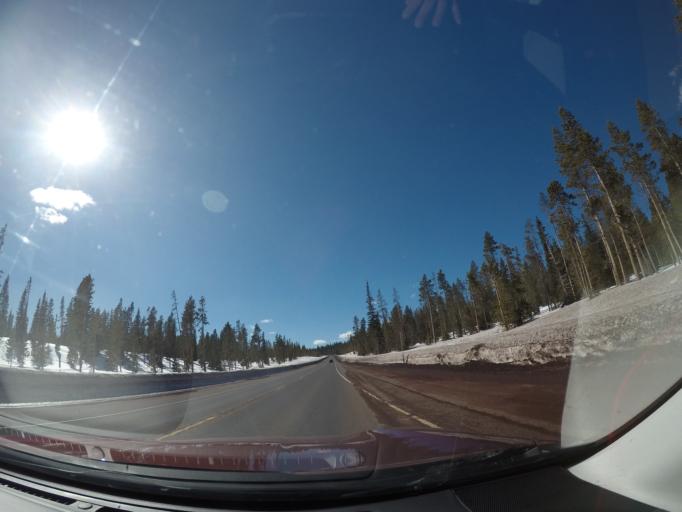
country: US
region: Oregon
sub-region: Deschutes County
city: Sunriver
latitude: 43.9877
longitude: -121.5692
